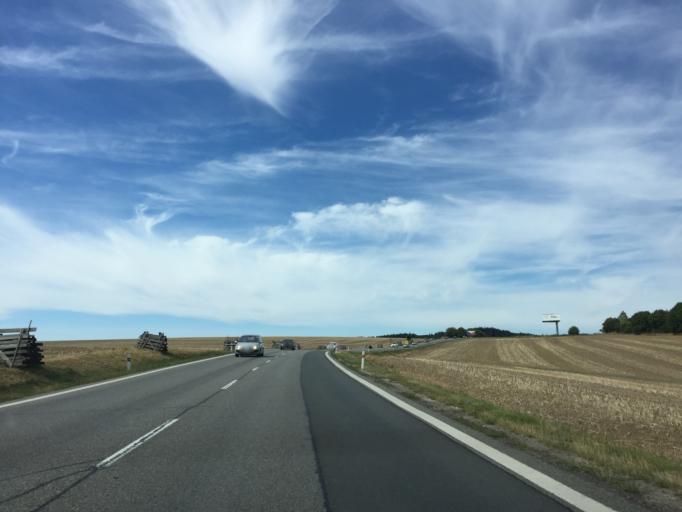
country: CZ
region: Jihocesky
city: Chotoviny
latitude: 49.5585
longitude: 14.6634
